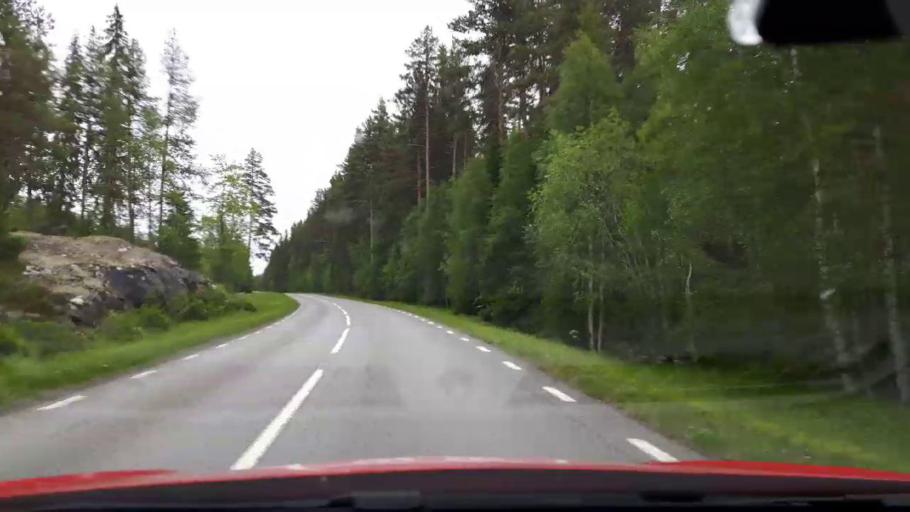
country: SE
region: Jaemtland
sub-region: Stroemsunds Kommun
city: Stroemsund
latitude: 63.4281
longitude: 15.5051
